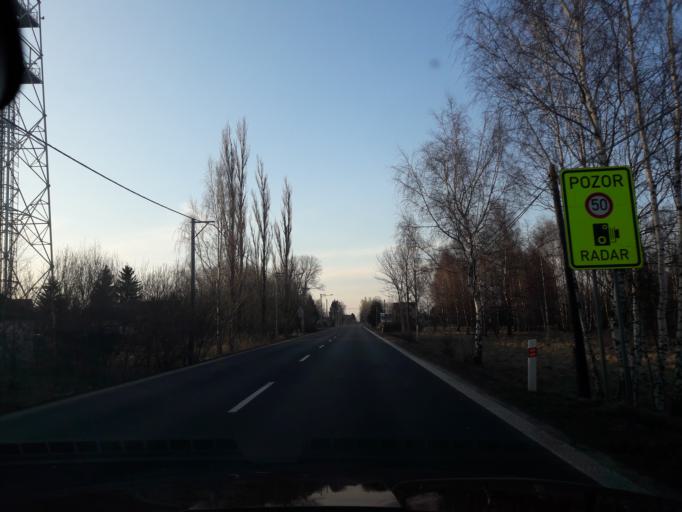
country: CZ
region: Ustecky
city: Dolni Podluzi
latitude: 50.8992
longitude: 14.5700
